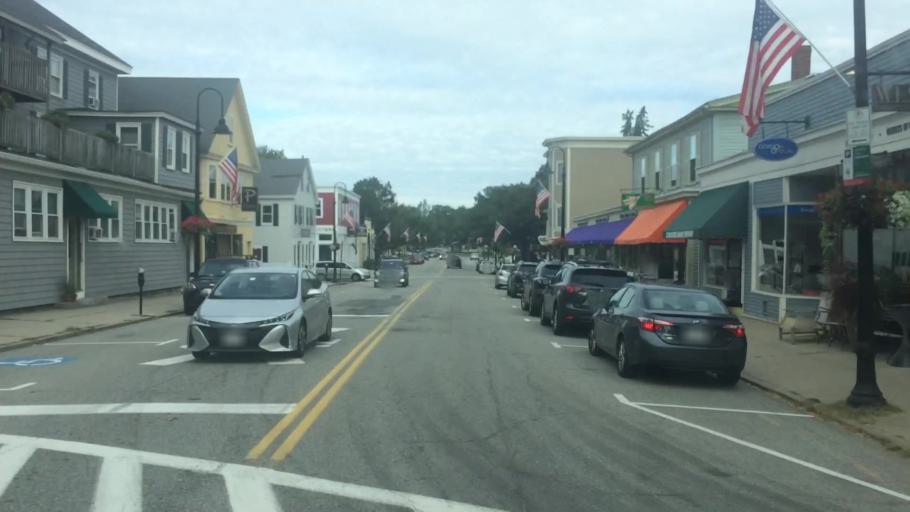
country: US
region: Massachusetts
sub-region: Middlesex County
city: West Concord
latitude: 42.4570
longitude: -71.3950
